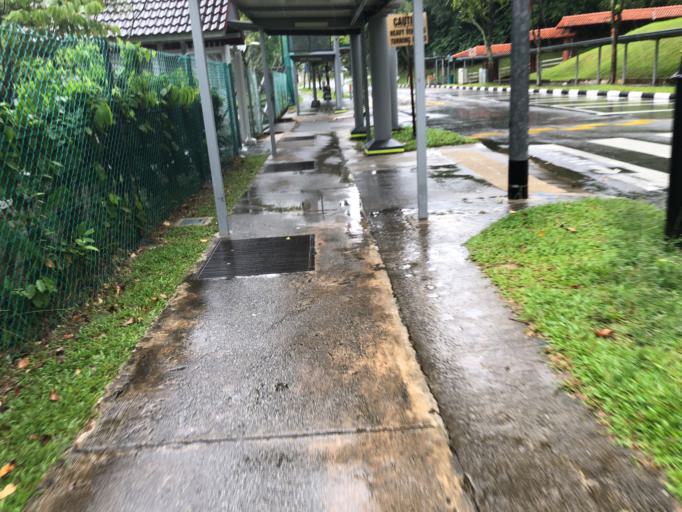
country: SG
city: Singapore
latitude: 1.3466
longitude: 103.7522
